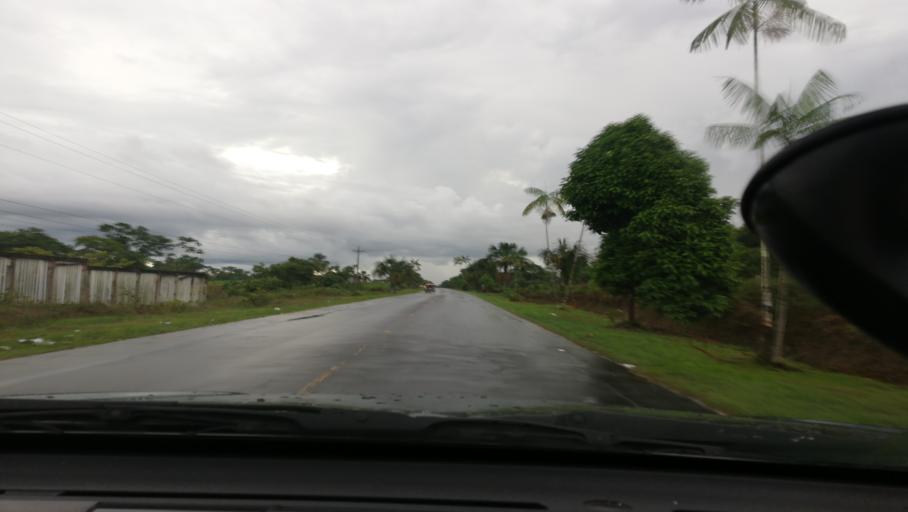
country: PE
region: Loreto
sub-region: Provincia de Maynas
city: Iquitos
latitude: -3.9020
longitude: -73.3535
